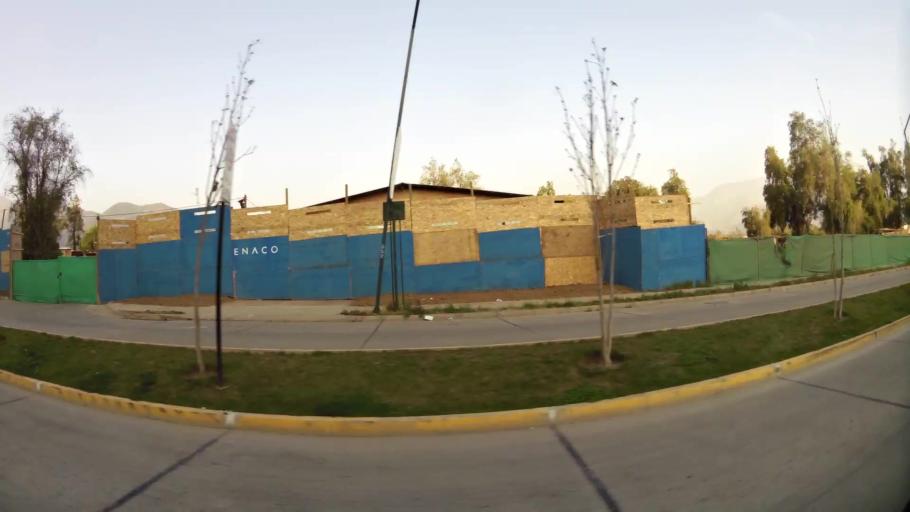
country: CL
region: Santiago Metropolitan
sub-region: Provincia de Chacabuco
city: Chicureo Abajo
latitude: -33.3251
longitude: -70.5189
